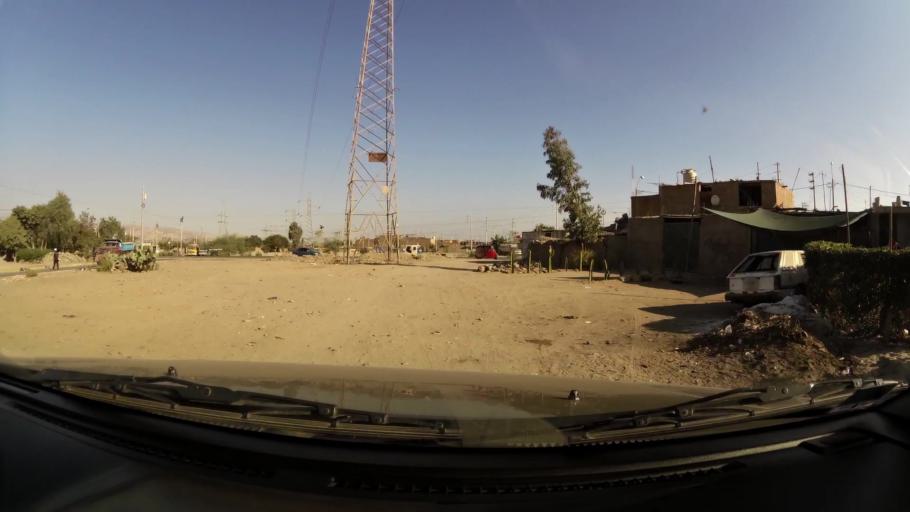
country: PE
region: Ica
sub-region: Provincia de Ica
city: La Tinguina
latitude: -14.0524
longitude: -75.6933
